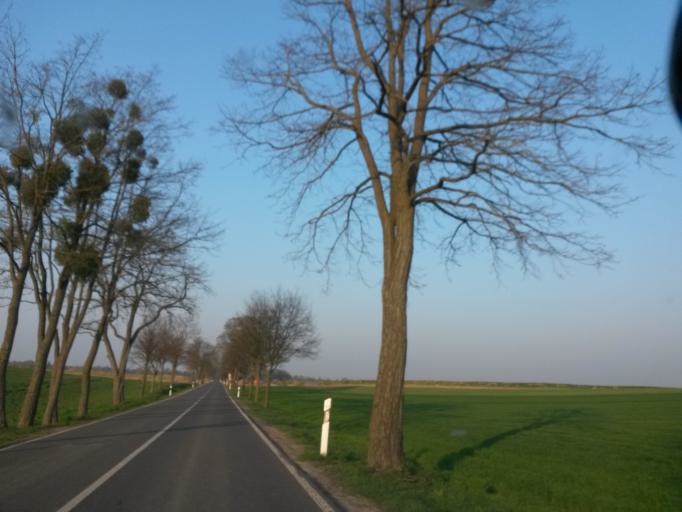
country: DE
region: Brandenburg
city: Rehfelde
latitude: 52.5590
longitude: 13.9569
